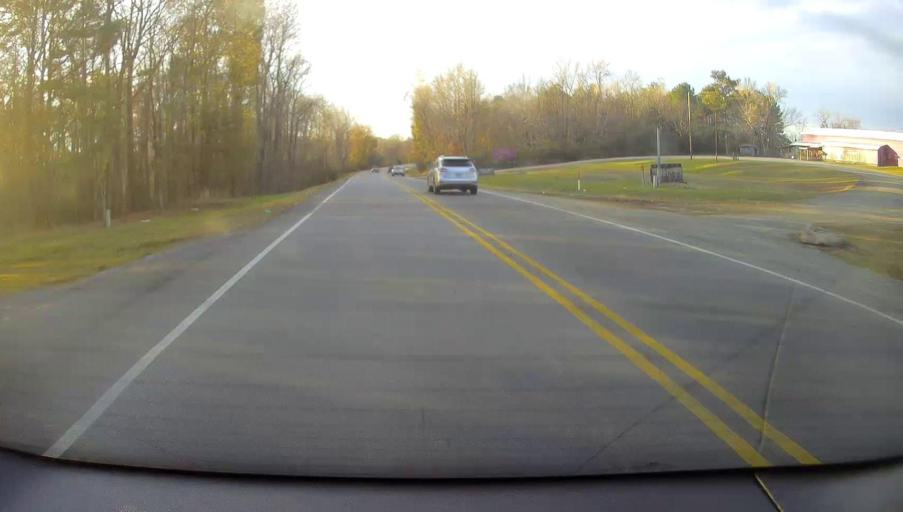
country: US
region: Alabama
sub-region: Blount County
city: Blountsville
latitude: 34.1422
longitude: -86.4456
